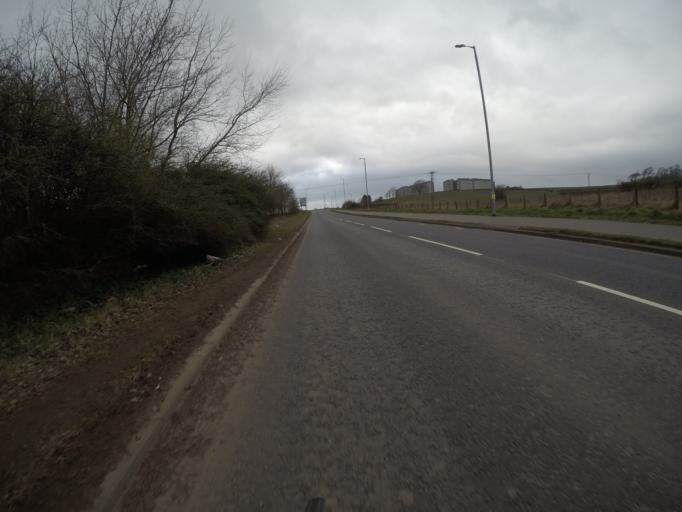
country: GB
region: Scotland
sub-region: East Ayrshire
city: Crosshouse
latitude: 55.6114
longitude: -4.5294
